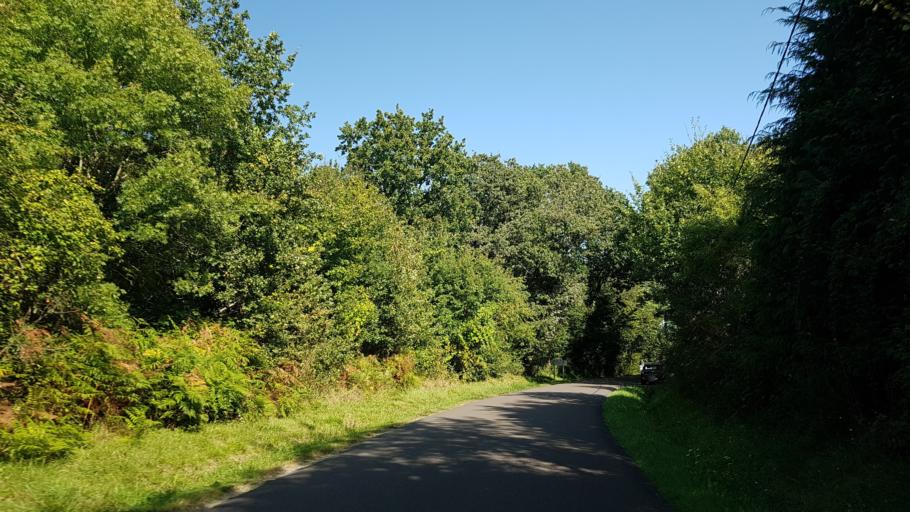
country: FR
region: Poitou-Charentes
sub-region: Departement de la Charente-Maritime
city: Breuillet
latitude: 45.7017
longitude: -1.0530
